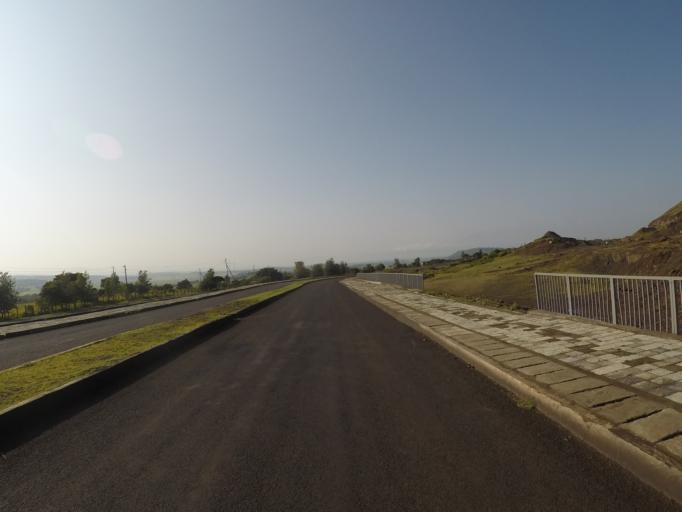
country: ET
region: Amhara
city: Gondar
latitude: 12.5272
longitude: 37.4301
